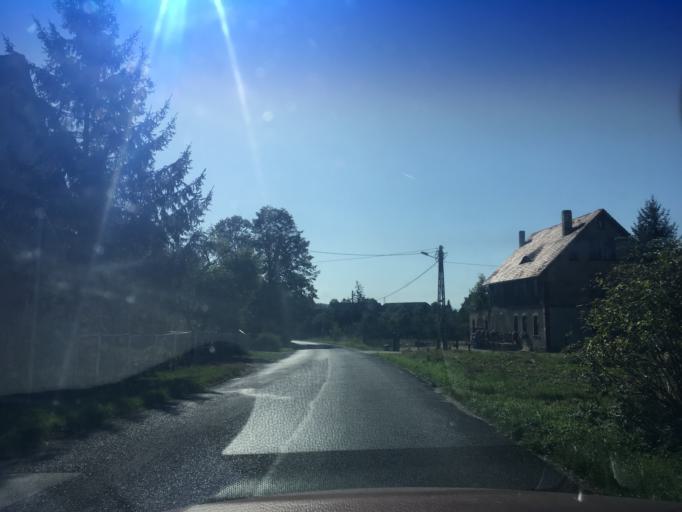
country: PL
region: Lower Silesian Voivodeship
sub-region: Powiat zgorzelecki
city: Sulikow
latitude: 51.1065
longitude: 15.0667
